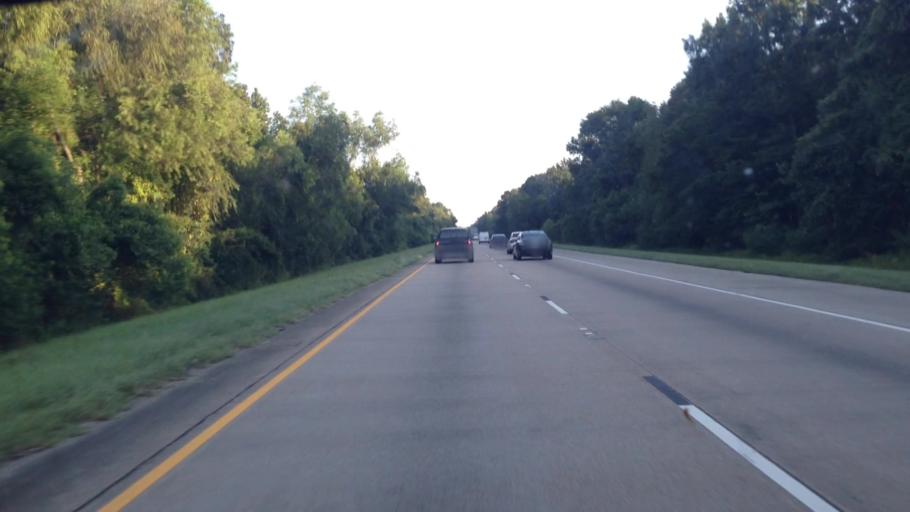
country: US
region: Louisiana
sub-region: Ascension Parish
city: Prairieville
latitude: 30.2900
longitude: -90.9903
